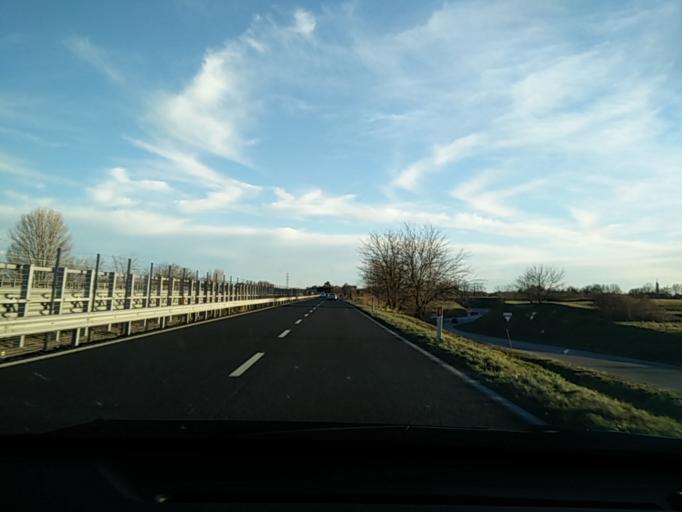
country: IT
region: Friuli Venezia Giulia
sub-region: Provincia di Udine
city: Passons
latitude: 46.0642
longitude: 13.1976
